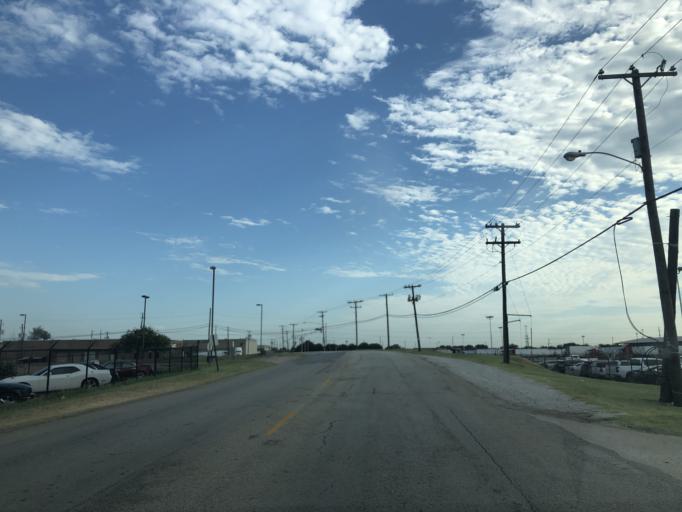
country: US
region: Texas
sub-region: Dallas County
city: Irving
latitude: 32.8093
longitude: -96.8895
